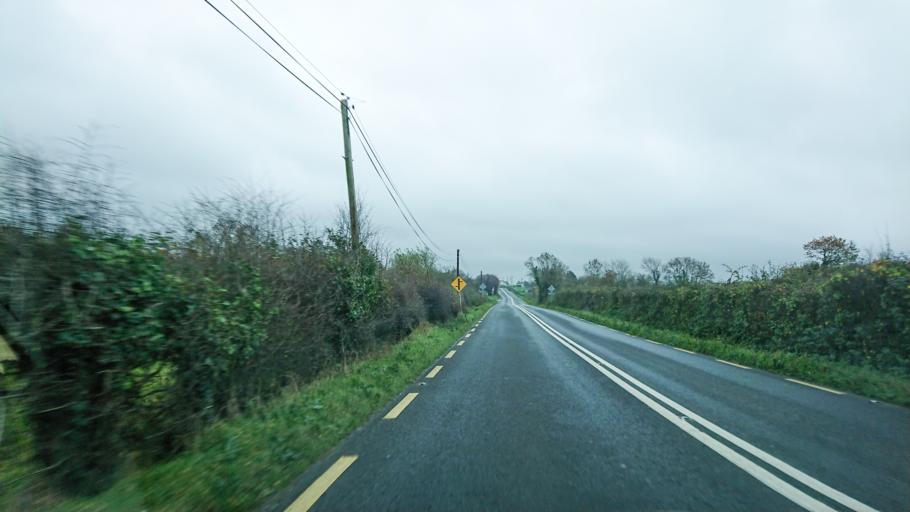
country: IE
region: Leinster
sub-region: Kilkenny
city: Mooncoin
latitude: 52.3064
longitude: -7.2812
